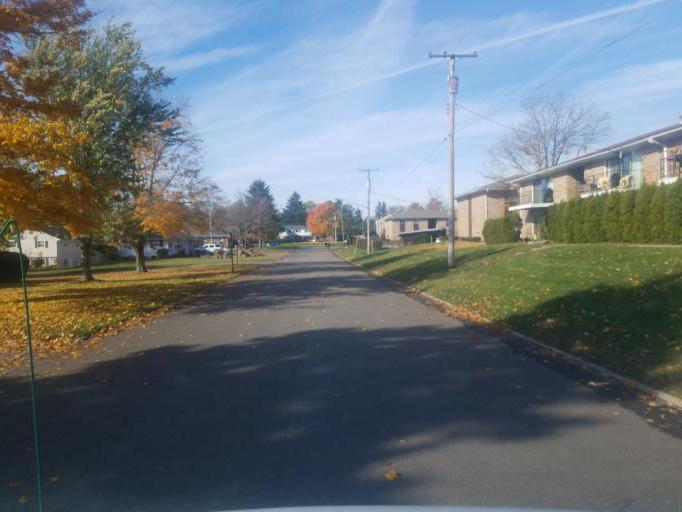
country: US
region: Ohio
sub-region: Richland County
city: Mansfield
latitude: 40.7321
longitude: -82.5297
